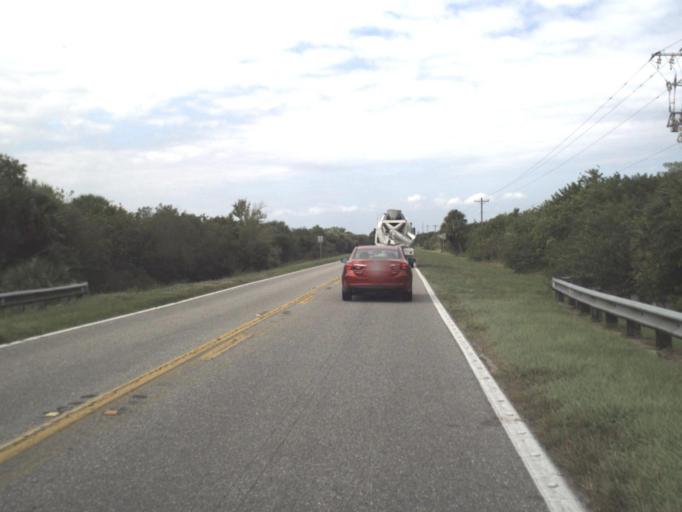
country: US
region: Florida
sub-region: Glades County
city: Moore Haven
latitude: 26.7684
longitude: -81.2147
